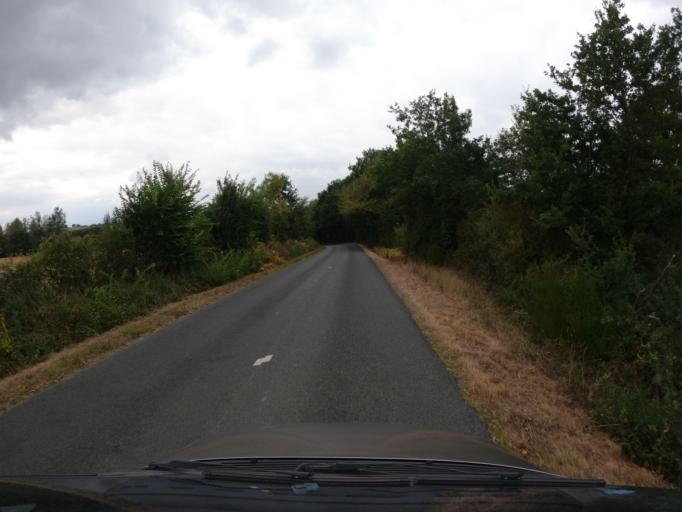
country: FR
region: Pays de la Loire
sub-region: Departement de Maine-et-Loire
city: Le Longeron
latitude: 46.9992
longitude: -1.0722
